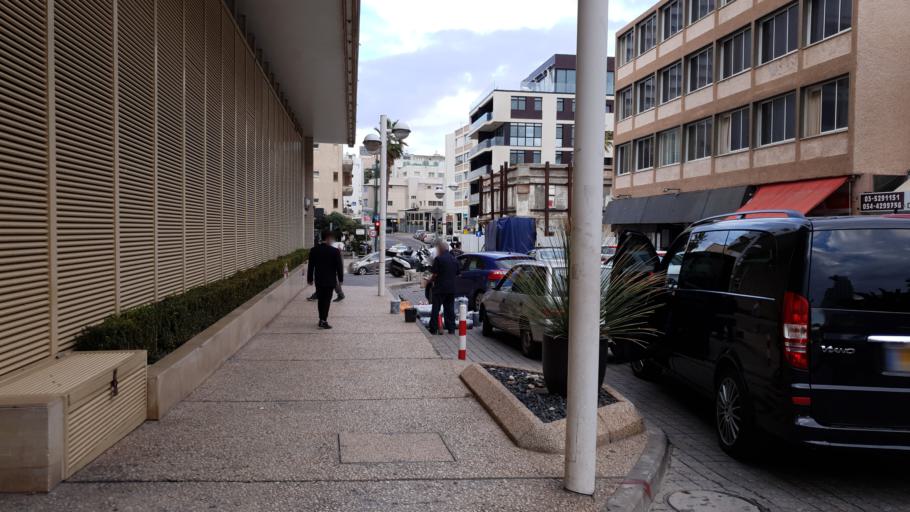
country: IL
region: Tel Aviv
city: Tel Aviv
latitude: 32.0795
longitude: 34.7680
